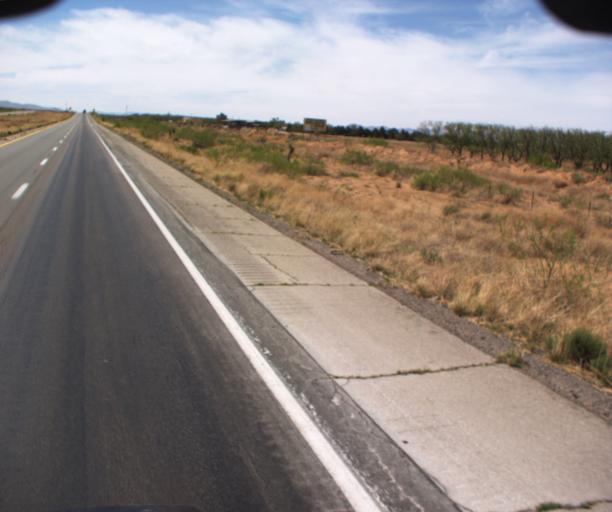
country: US
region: Arizona
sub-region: Cochise County
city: Willcox
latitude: 32.3176
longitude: -109.4783
